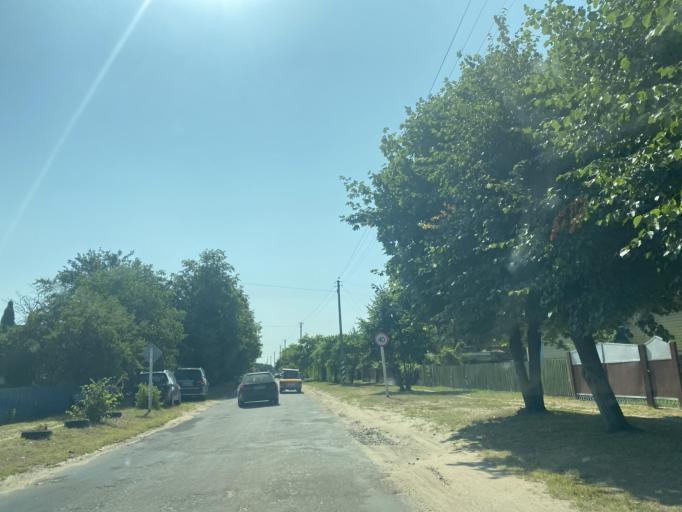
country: BY
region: Brest
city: Ivanava
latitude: 52.3129
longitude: 25.6167
